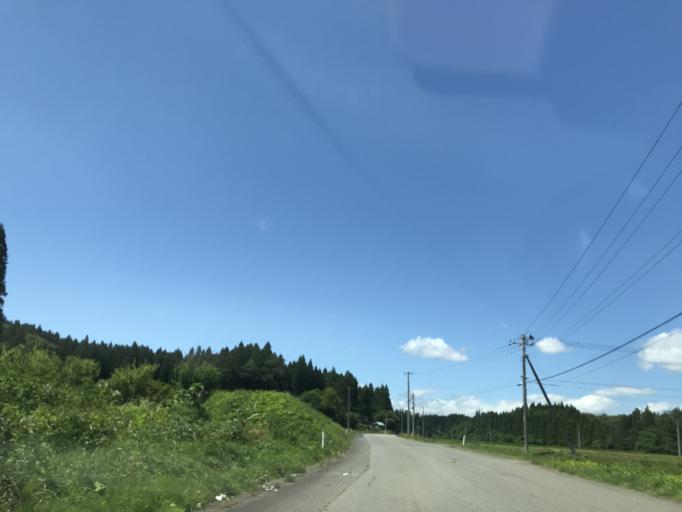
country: JP
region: Iwate
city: Ichinoseki
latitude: 38.9272
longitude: 141.0197
